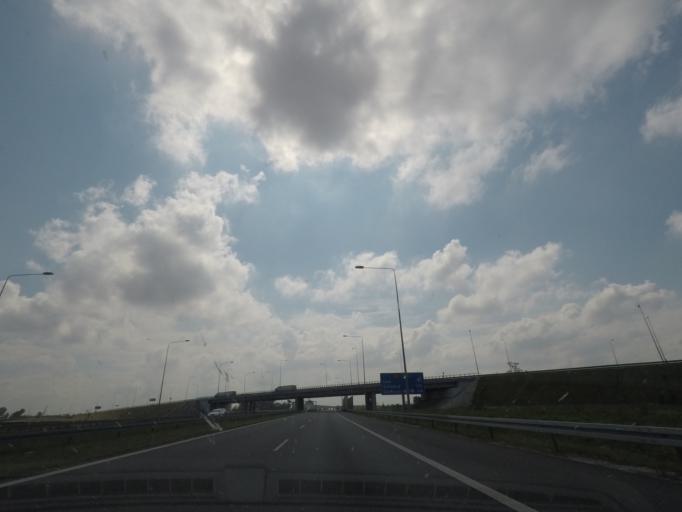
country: PL
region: Lodz Voivodeship
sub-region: Powiat kutnowski
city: Krzyzanow
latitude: 52.2200
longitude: 19.4713
